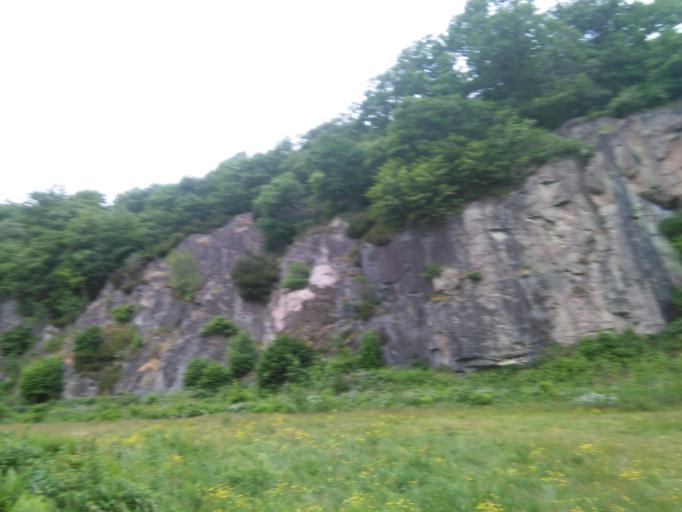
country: DK
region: Capital Region
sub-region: Bornholm Kommune
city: Akirkeby
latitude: 55.1102
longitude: 14.9037
